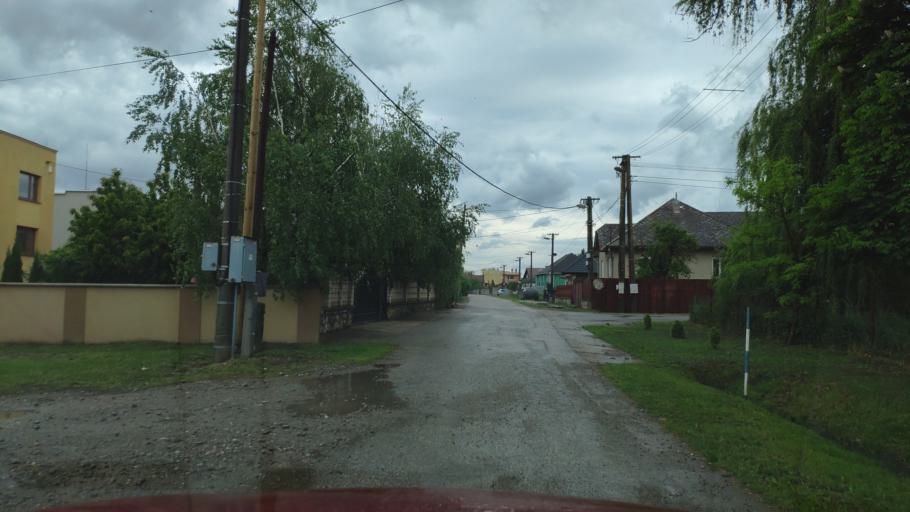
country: SK
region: Kosicky
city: Moldava nad Bodvou
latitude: 48.5705
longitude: 21.1217
